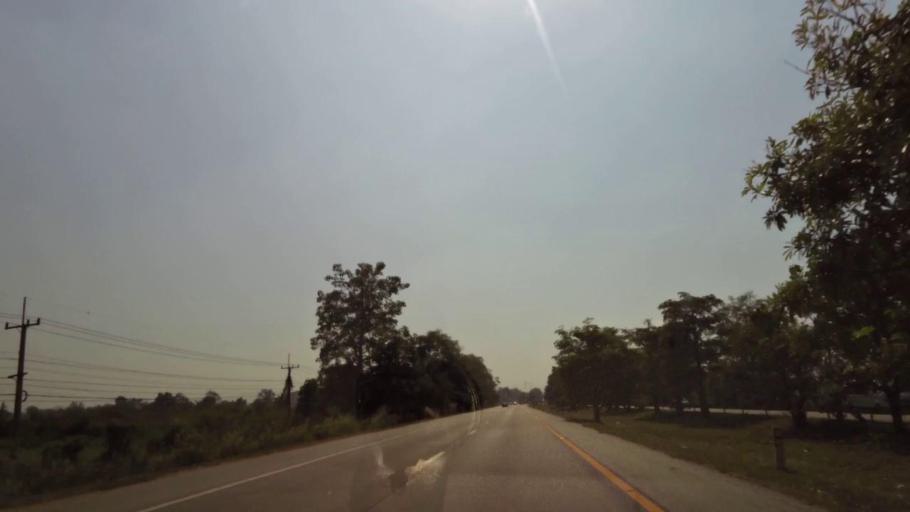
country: TH
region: Phichit
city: Wachira Barami
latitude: 16.6248
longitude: 100.1499
